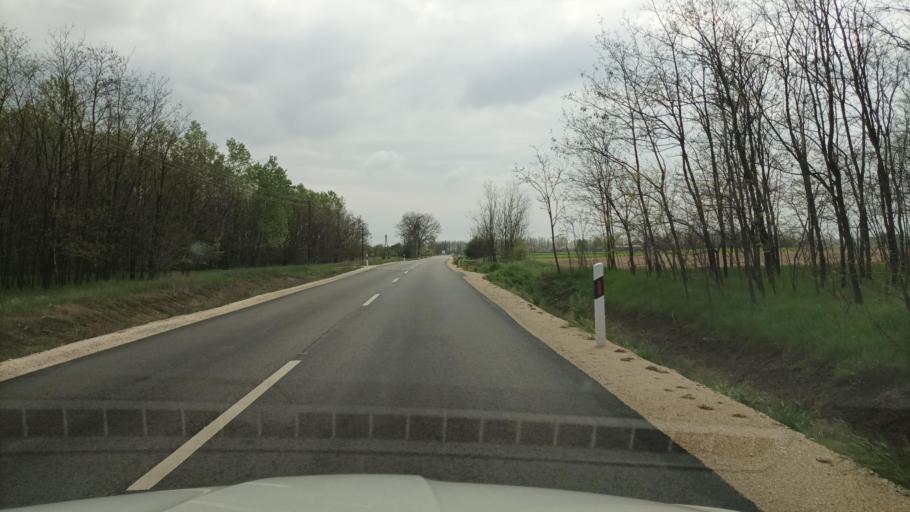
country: HU
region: Pest
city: Kocser
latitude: 47.0137
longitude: 19.8737
